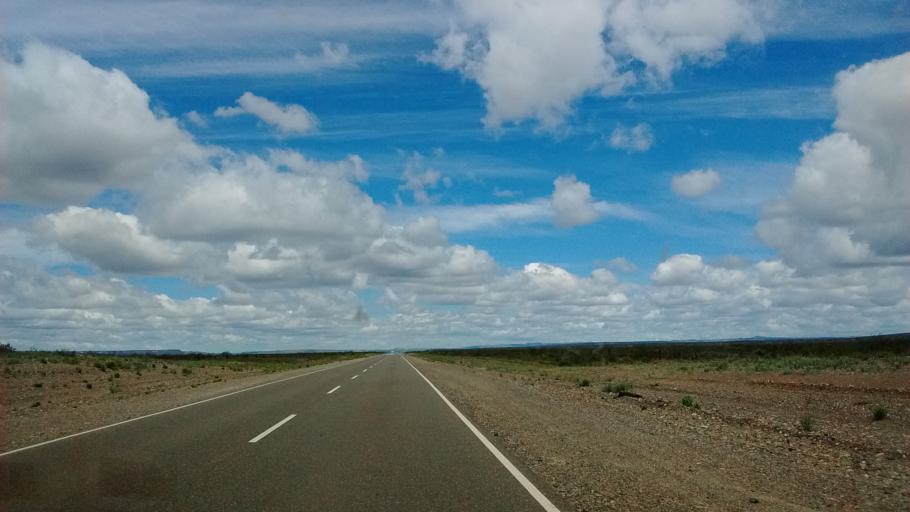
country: AR
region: Neuquen
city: Piedra del Aguila
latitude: -39.8141
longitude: -69.7221
